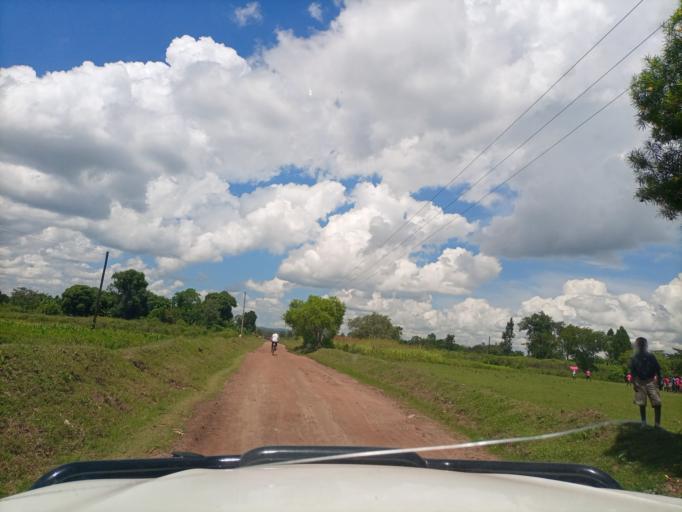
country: UG
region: Eastern Region
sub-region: Tororo District
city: Tororo
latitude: 0.6477
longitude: 33.9963
